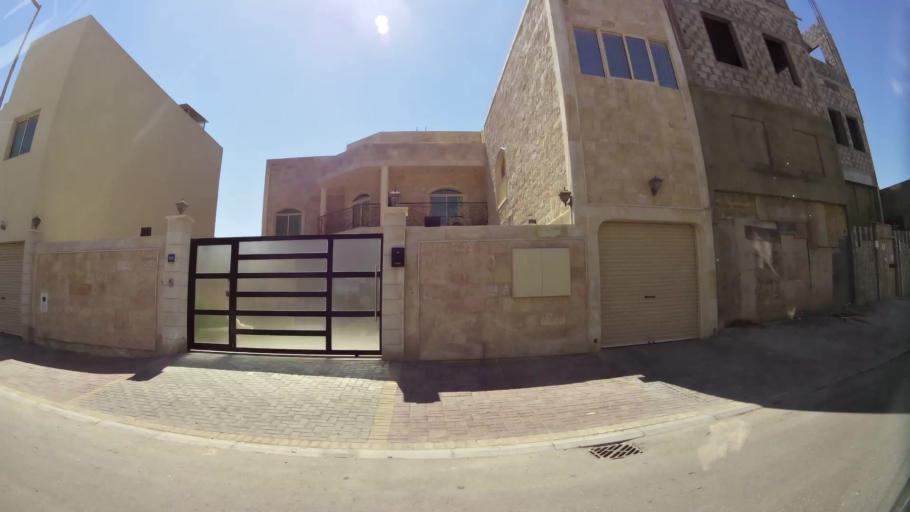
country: BH
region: Muharraq
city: Al Muharraq
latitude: 26.2837
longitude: 50.6369
